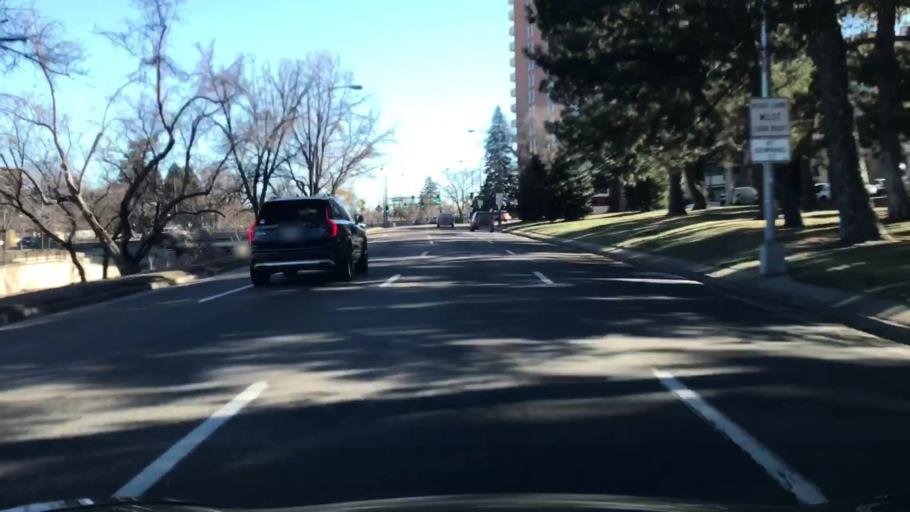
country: US
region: Colorado
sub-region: Denver County
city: Denver
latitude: 39.7187
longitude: -104.9758
